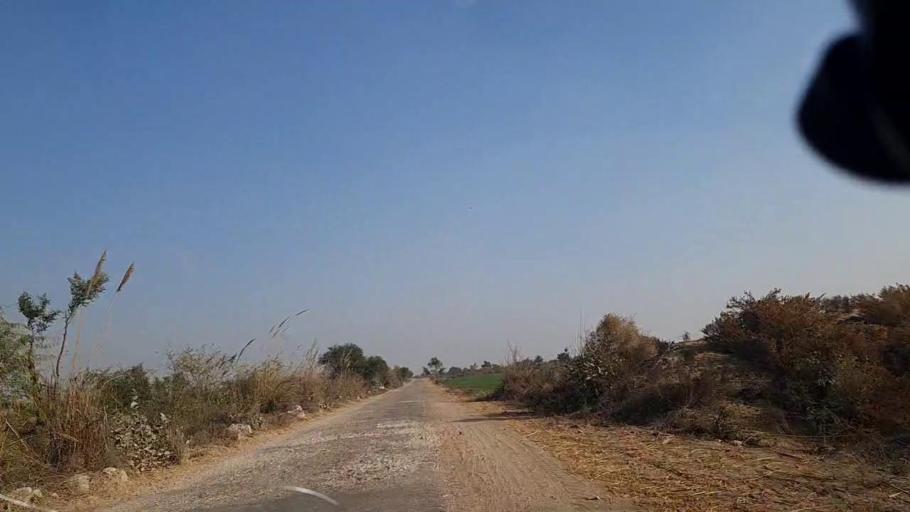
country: PK
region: Sindh
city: Khanpur
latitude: 27.6849
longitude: 69.5270
